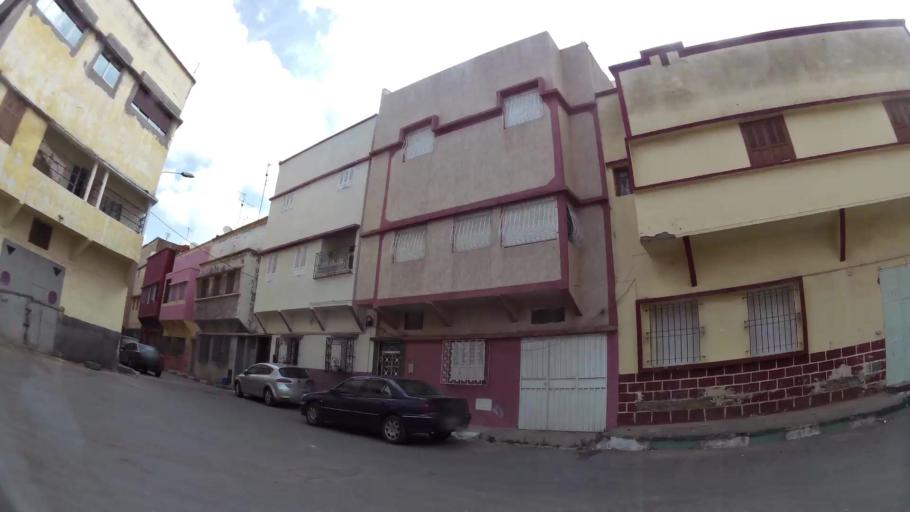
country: MA
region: Gharb-Chrarda-Beni Hssen
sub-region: Kenitra Province
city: Kenitra
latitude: 34.2586
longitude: -6.5675
